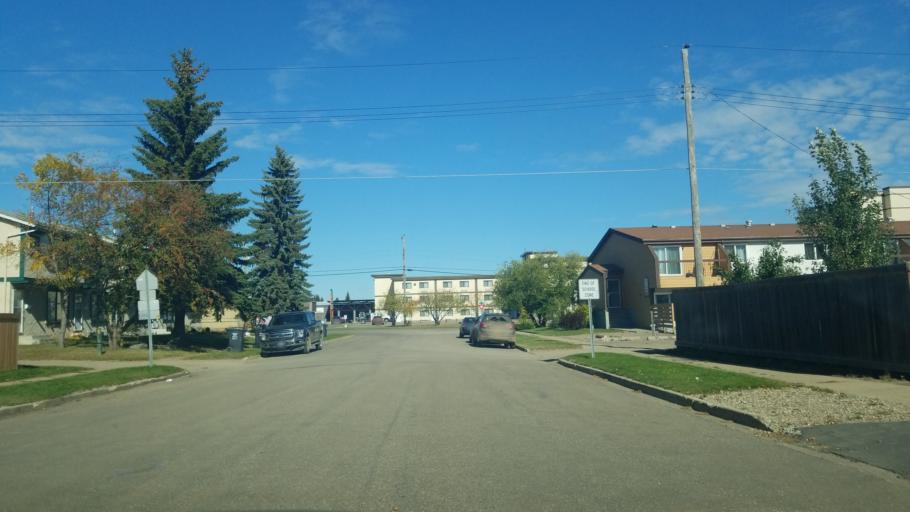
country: CA
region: Saskatchewan
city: Lloydminster
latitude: 53.2762
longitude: -110.0225
